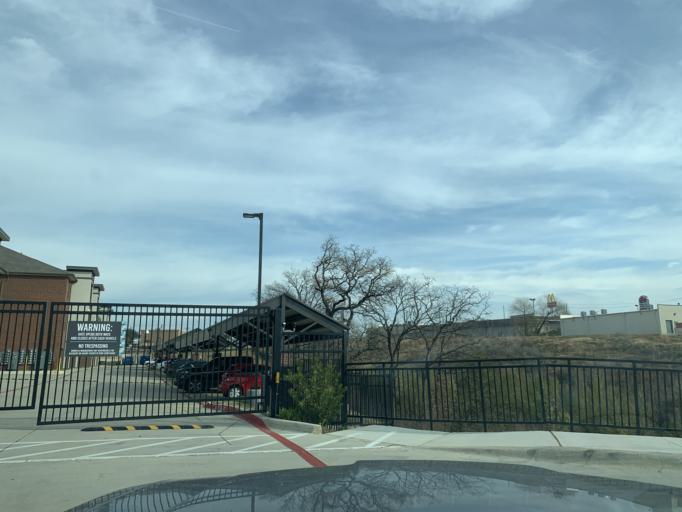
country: US
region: Texas
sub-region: Tarrant County
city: Euless
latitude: 32.7869
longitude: -97.0623
